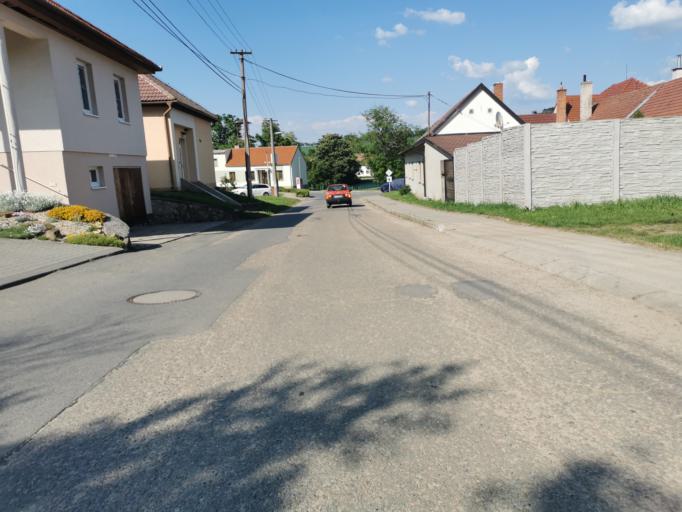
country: CZ
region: South Moravian
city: Straznice
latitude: 48.8587
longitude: 17.3427
